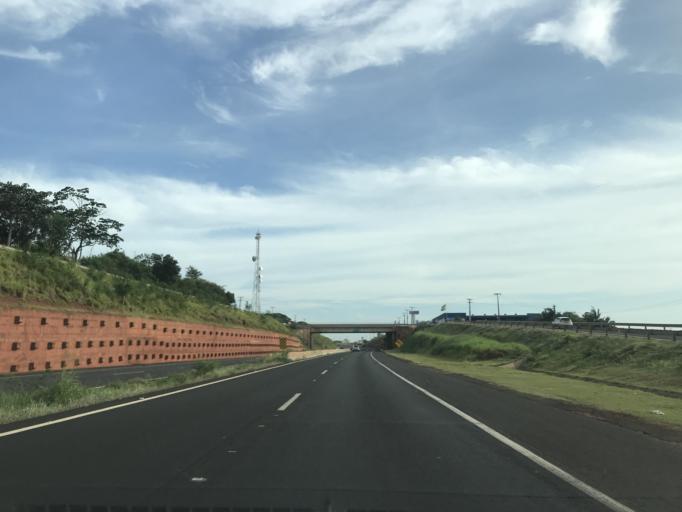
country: BR
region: Parana
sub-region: Mandaguacu
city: Mandaguacu
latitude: -23.3229
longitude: -52.1108
